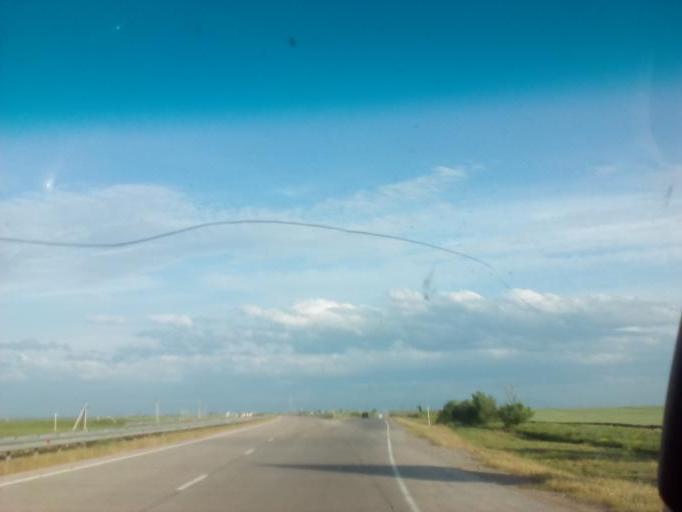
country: KZ
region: Ongtustik Qazaqstan
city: Temirlanovka
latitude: 42.5353
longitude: 69.3350
